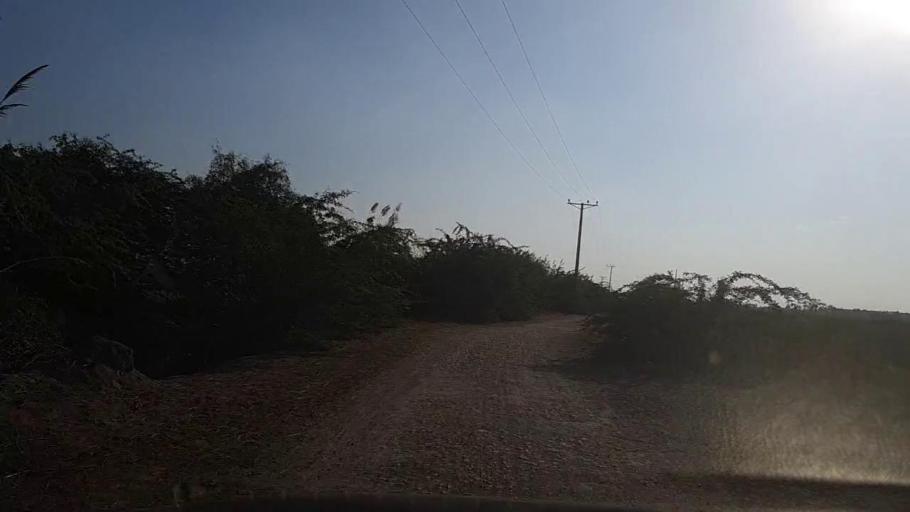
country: PK
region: Sindh
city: Gharo
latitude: 24.7123
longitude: 67.6849
